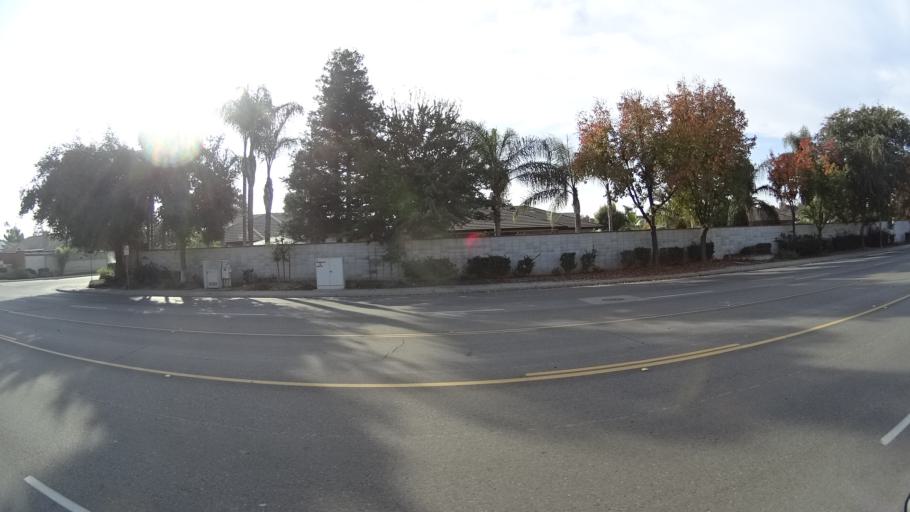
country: US
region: California
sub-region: Kern County
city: Greenacres
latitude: 35.3690
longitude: -119.1235
